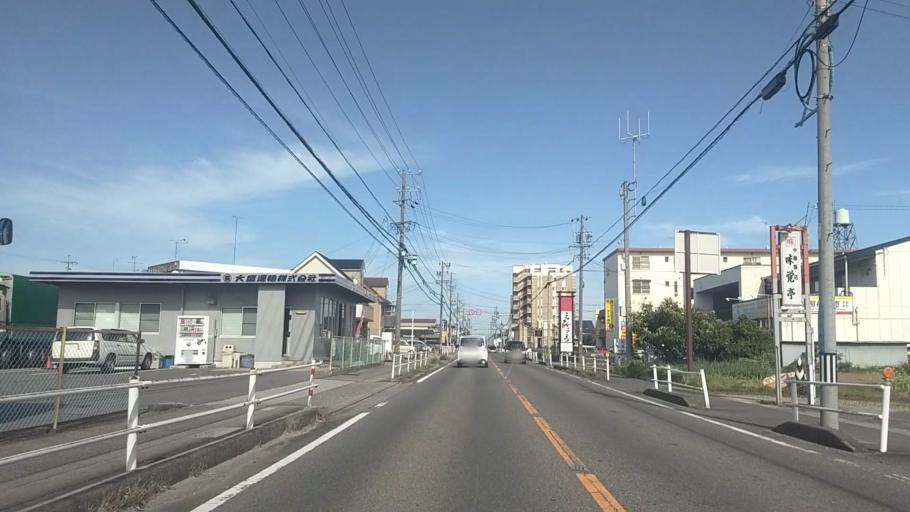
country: JP
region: Aichi
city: Anjo
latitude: 34.9587
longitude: 137.0948
